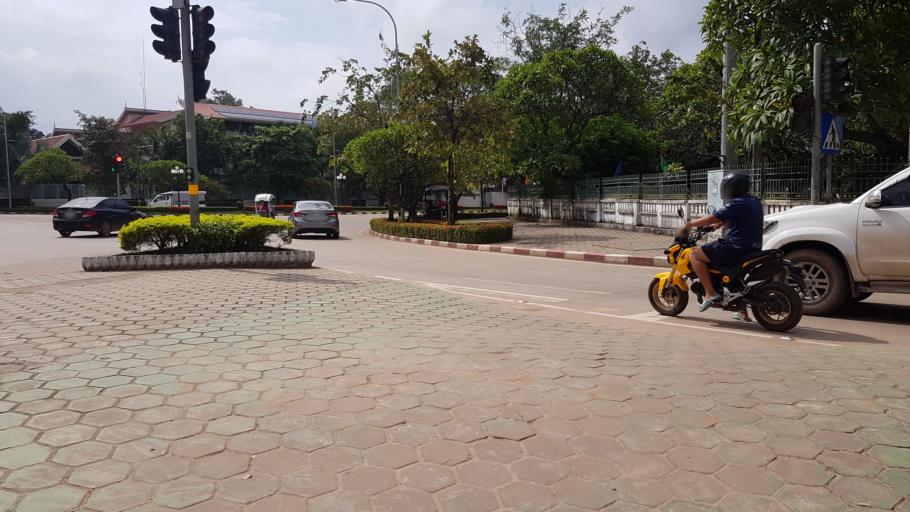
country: LA
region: Vientiane
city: Vientiane
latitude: 17.9706
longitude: 102.6179
